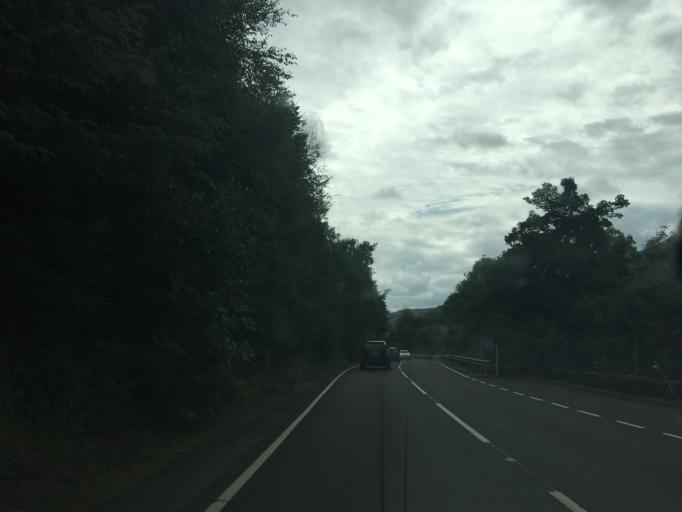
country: GB
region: Scotland
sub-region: Stirling
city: Callander
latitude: 56.2868
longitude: -4.2839
